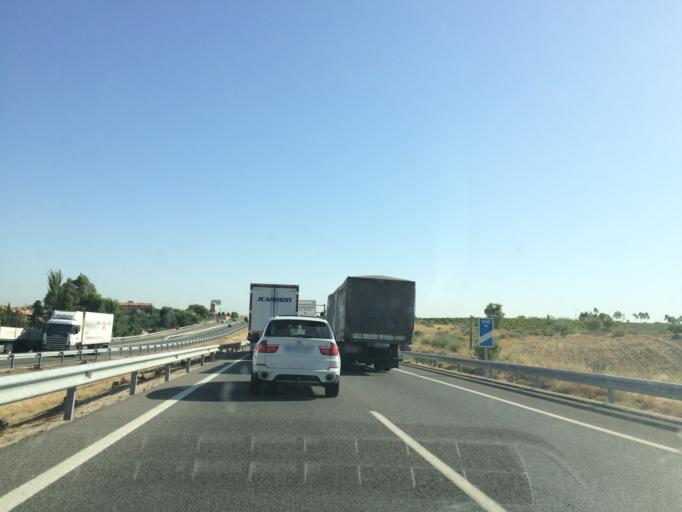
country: ES
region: Castille-La Mancha
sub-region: Province of Toledo
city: Valmojado
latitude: 40.2383
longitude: -4.0631
